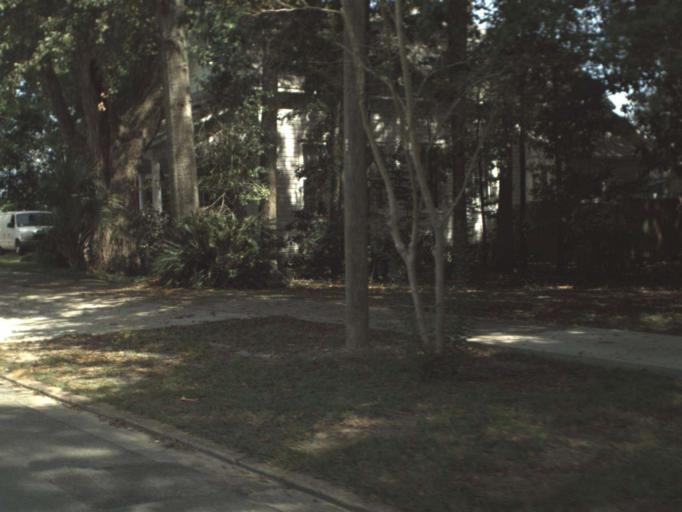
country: US
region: Florida
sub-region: Washington County
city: Chipley
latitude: 30.7781
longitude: -85.5382
